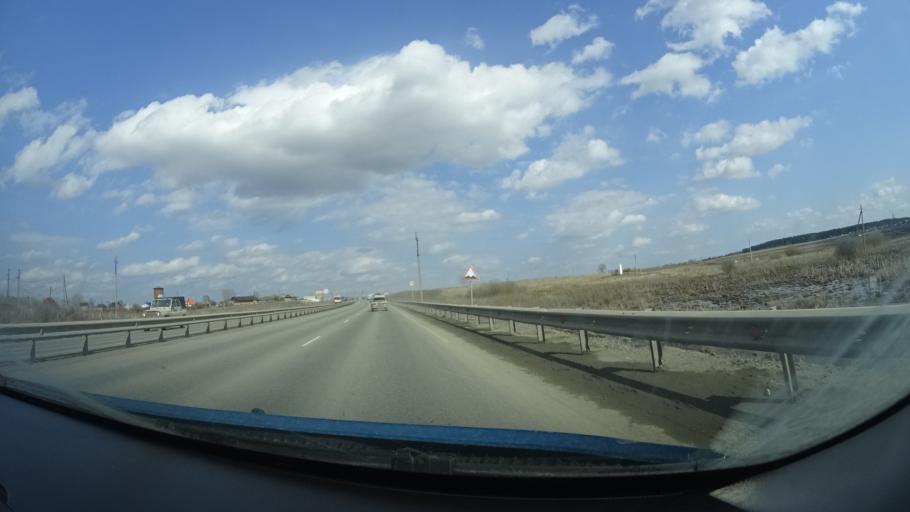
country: RU
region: Perm
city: Kultayevo
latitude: 57.9051
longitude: 55.9844
